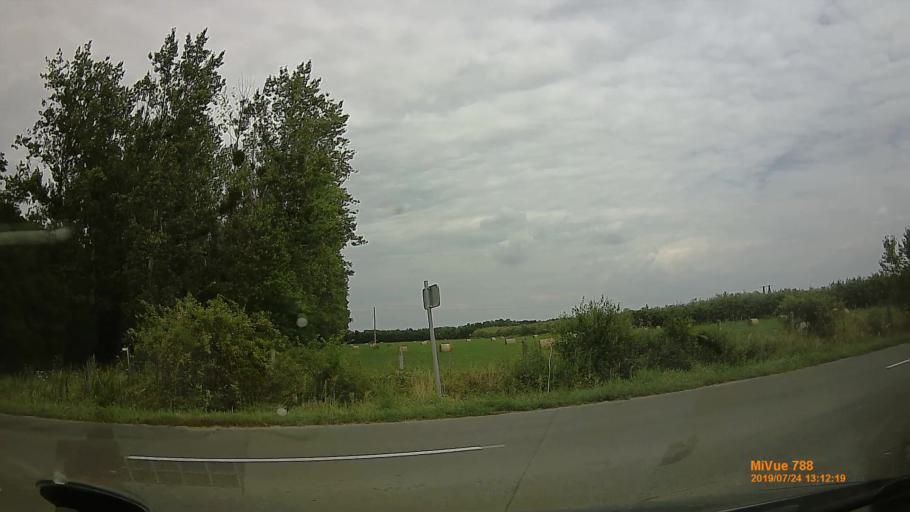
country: HU
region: Szabolcs-Szatmar-Bereg
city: Vasarosnameny
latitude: 48.1622
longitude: 22.3405
